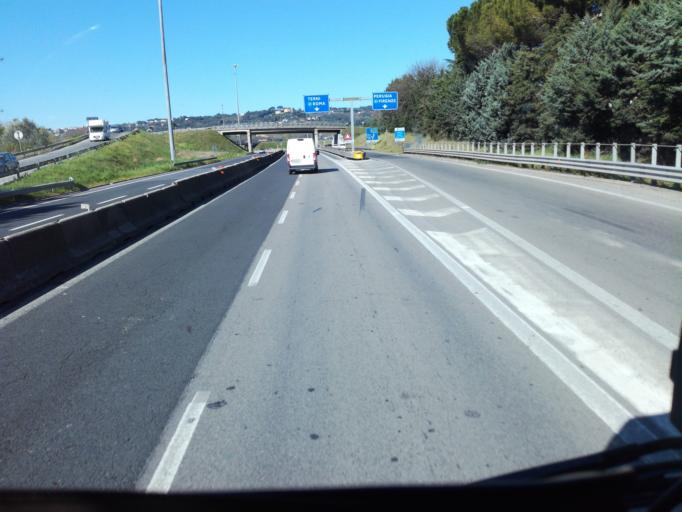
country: IT
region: Umbria
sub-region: Provincia di Perugia
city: Via Lippia
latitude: 43.0860
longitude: 12.4351
